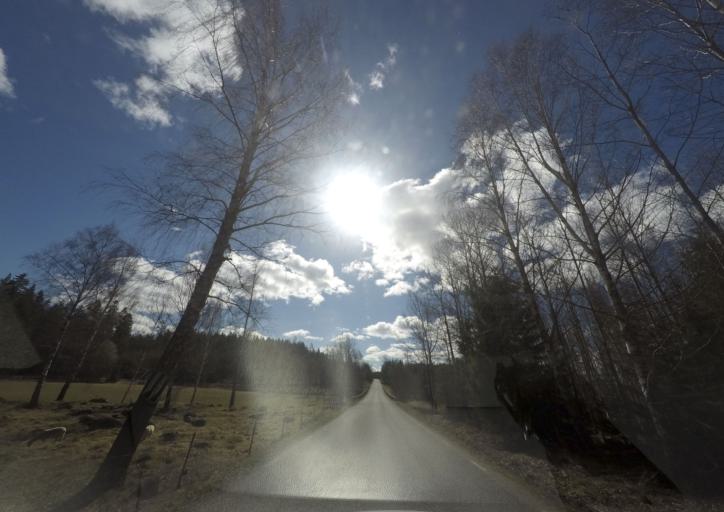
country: SE
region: OEstergoetland
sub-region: Norrkopings Kommun
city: Krokek
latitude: 58.7937
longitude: 16.4583
